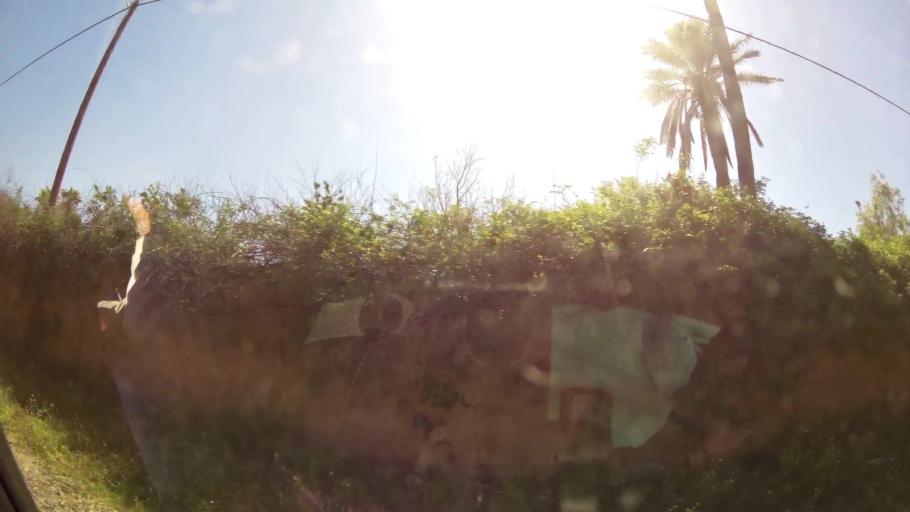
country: MA
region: Marrakech-Tensift-Al Haouz
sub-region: Marrakech
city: Marrakesh
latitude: 31.6628
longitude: -7.9584
